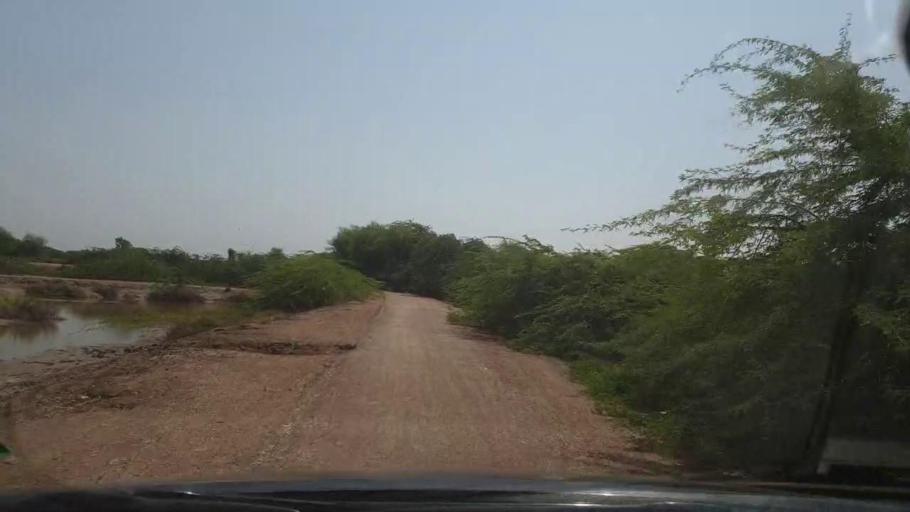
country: PK
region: Sindh
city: Tando Bago
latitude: 24.7992
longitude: 69.1558
